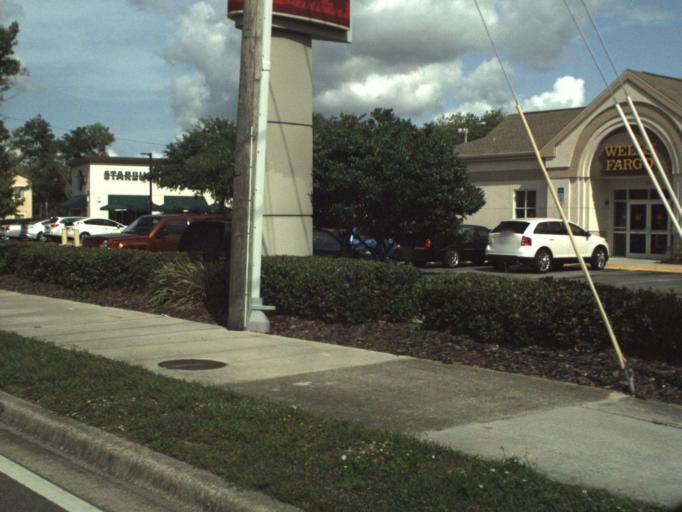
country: US
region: Florida
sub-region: Orange County
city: Winter Park
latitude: 28.6019
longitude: -81.3187
